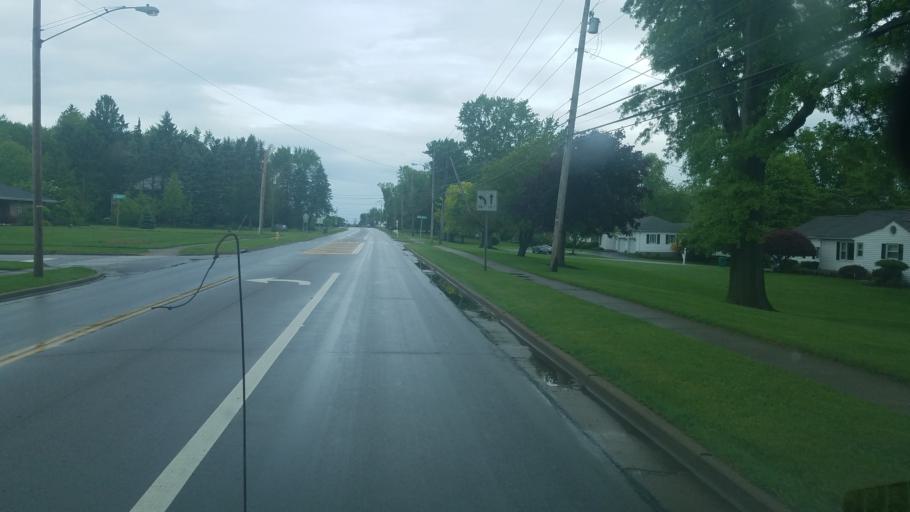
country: US
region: Ohio
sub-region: Wayne County
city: Wooster
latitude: 40.8367
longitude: -81.9391
